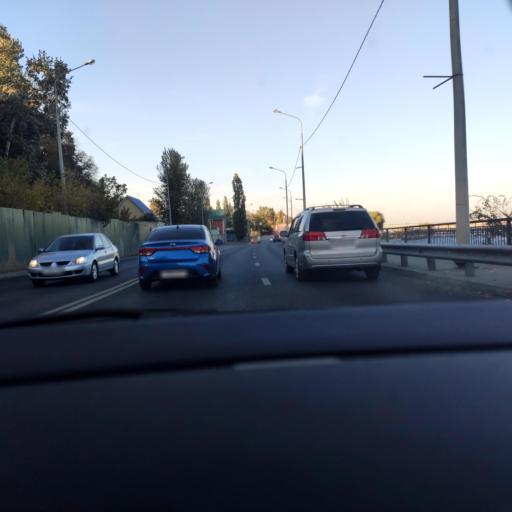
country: RU
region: Voronezj
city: Voronezh
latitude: 51.6825
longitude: 39.2282
